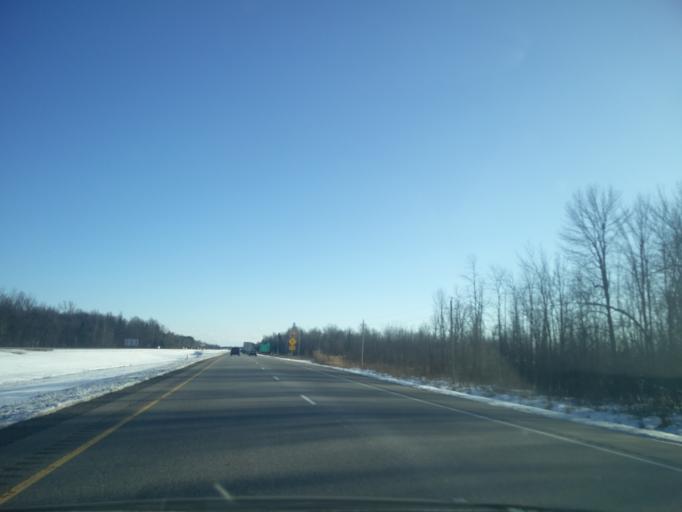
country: CA
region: Ontario
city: Bells Corners
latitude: 45.0451
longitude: -75.6237
